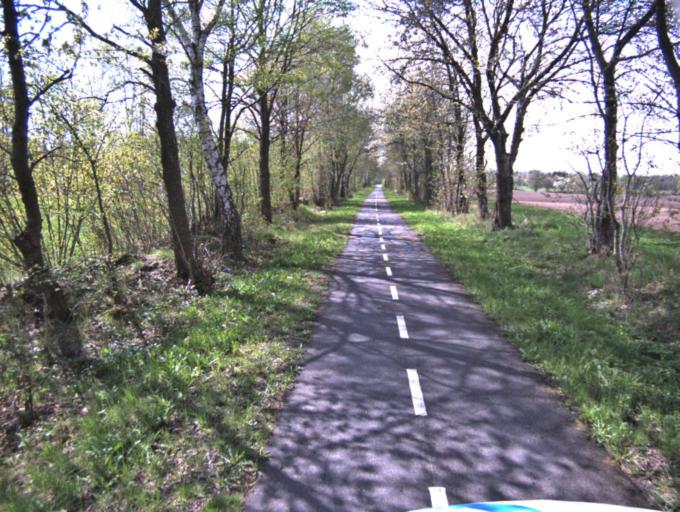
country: SE
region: Skane
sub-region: Kristianstads Kommun
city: Onnestad
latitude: 56.0032
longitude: 14.0471
